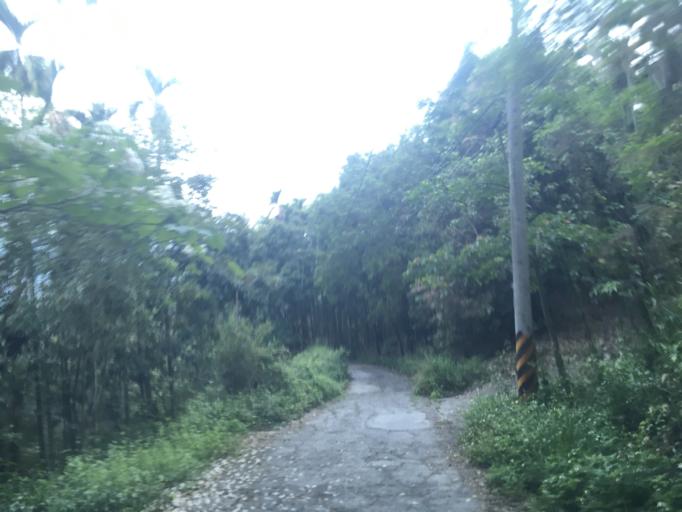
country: TW
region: Taiwan
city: Zhongxing New Village
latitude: 24.0490
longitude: 120.8061
